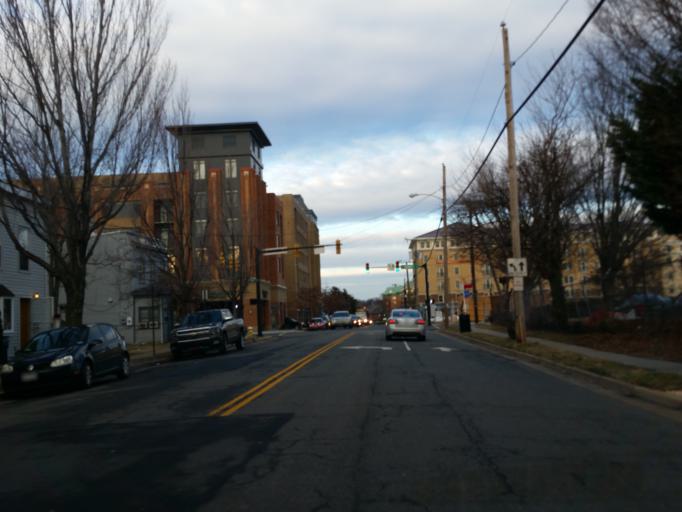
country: US
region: Virginia
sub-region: City of Alexandria
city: Alexandria
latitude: 38.8113
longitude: -77.0494
